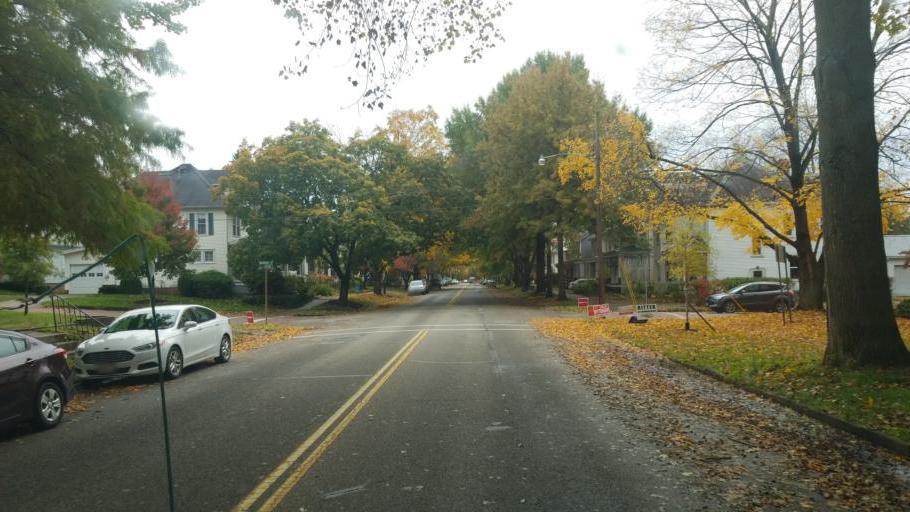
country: US
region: Ohio
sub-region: Washington County
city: Marietta
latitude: 39.4252
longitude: -81.4604
